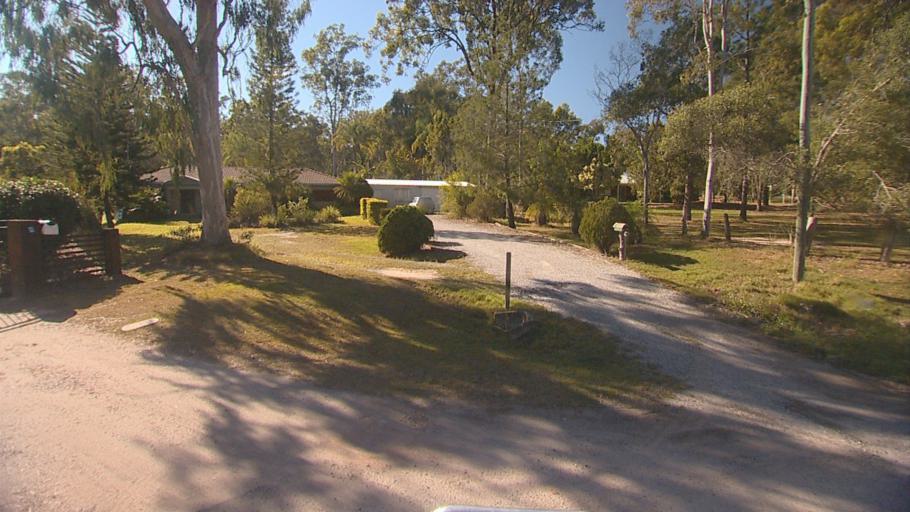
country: AU
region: Queensland
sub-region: Logan
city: Chambers Flat
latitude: -27.7842
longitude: 153.1257
